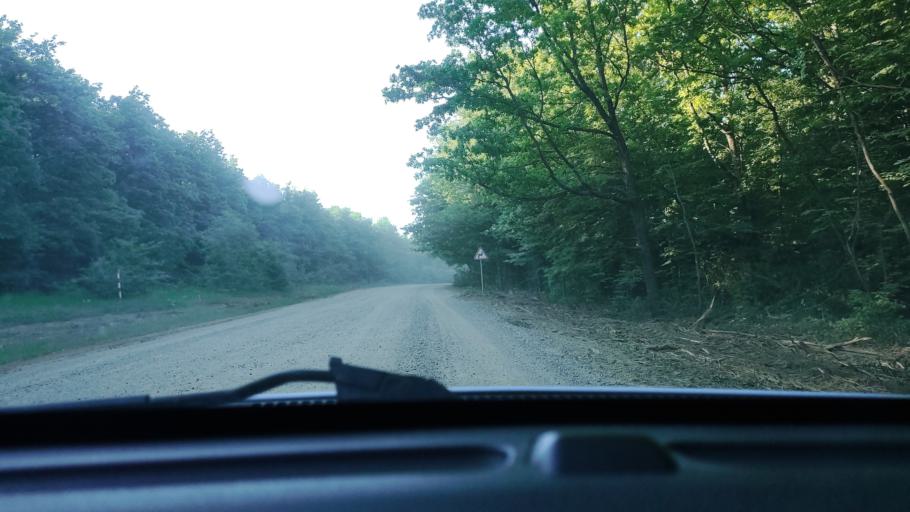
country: RU
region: Krasnodarskiy
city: Goryachiy Klyuch
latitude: 44.7153
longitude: 38.9914
